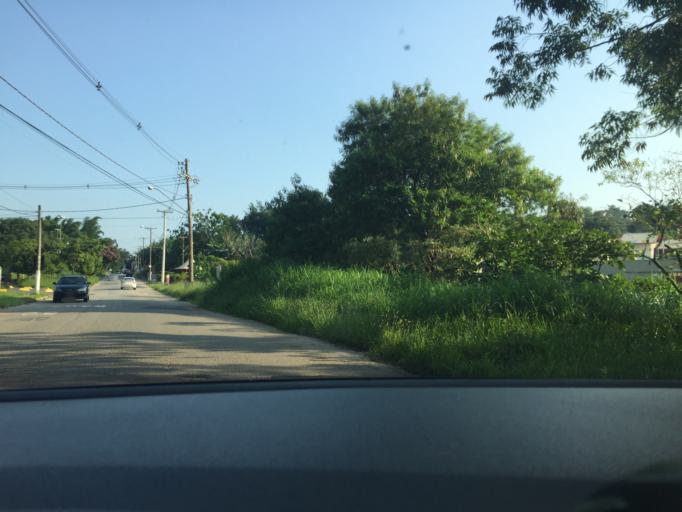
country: BR
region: Sao Paulo
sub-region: Vinhedo
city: Vinhedo
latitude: -23.0089
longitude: -47.0091
